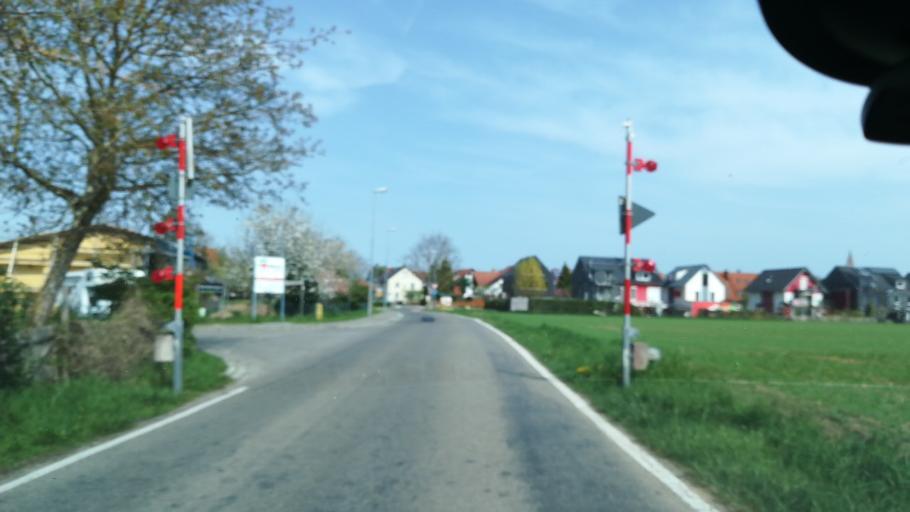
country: DE
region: Baden-Wuerttemberg
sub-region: Tuebingen Region
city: Uberlingen
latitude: 47.7387
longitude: 9.1512
